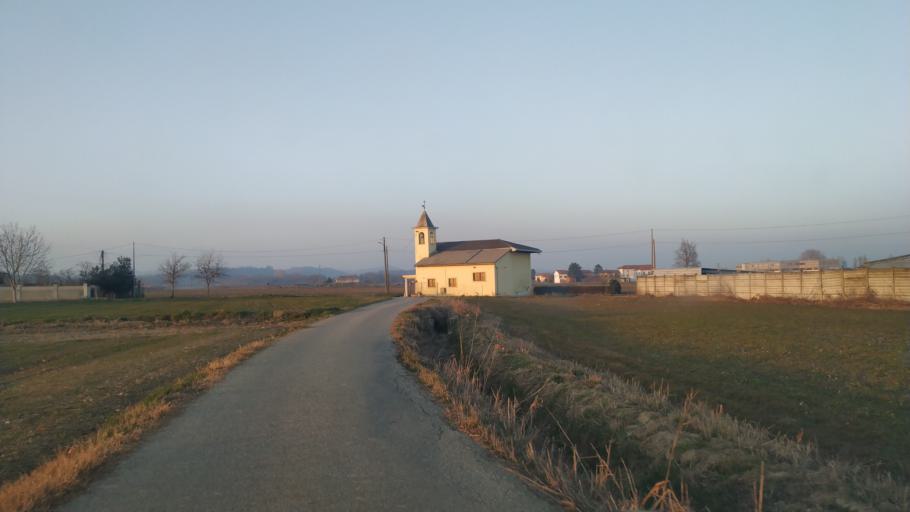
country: IT
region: Piedmont
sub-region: Provincia di Vercelli
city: Cigliano
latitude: 45.3146
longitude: 8.0148
